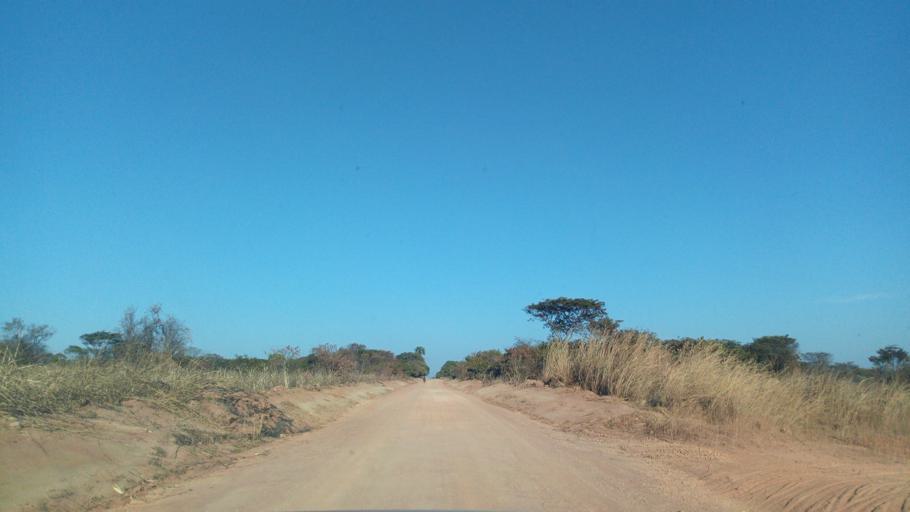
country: ZM
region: Luapula
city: Mwense
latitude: -10.4458
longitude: 28.5681
